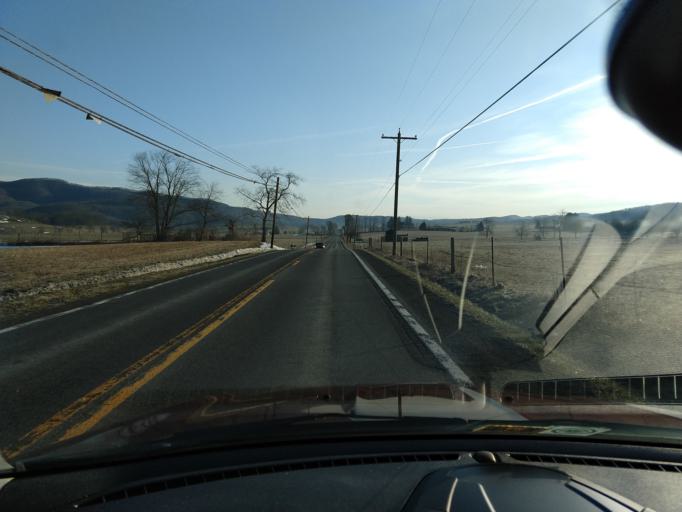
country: US
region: West Virginia
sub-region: Pocahontas County
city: Marlinton
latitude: 38.1434
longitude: -80.2000
